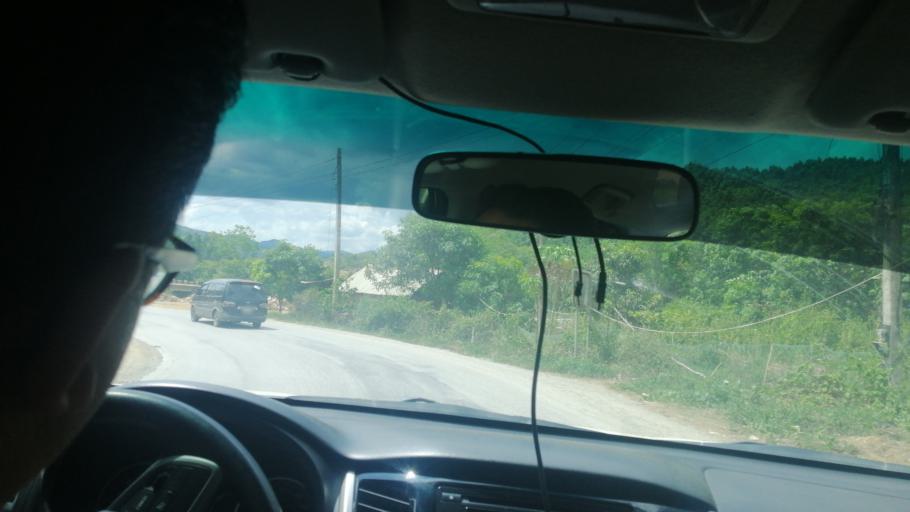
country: LA
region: Loungnamtha
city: Louang Namtha
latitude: 21.0414
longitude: 101.6507
